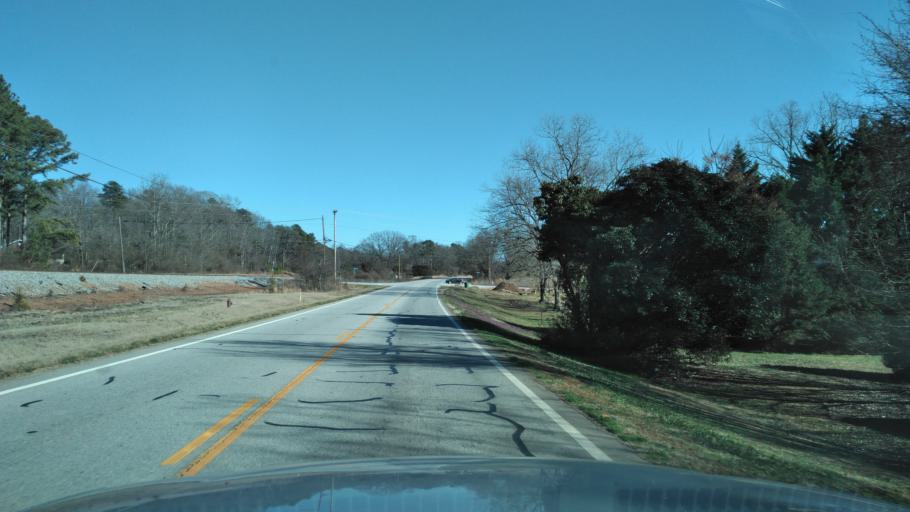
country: US
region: Georgia
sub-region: Banks County
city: Maysville
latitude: 34.2395
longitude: -83.5167
